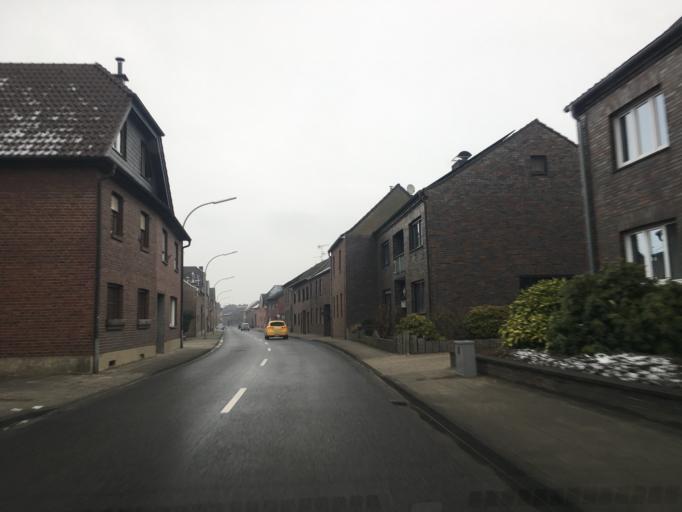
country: DE
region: North Rhine-Westphalia
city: Huckelhoven
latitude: 51.1027
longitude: 6.2393
